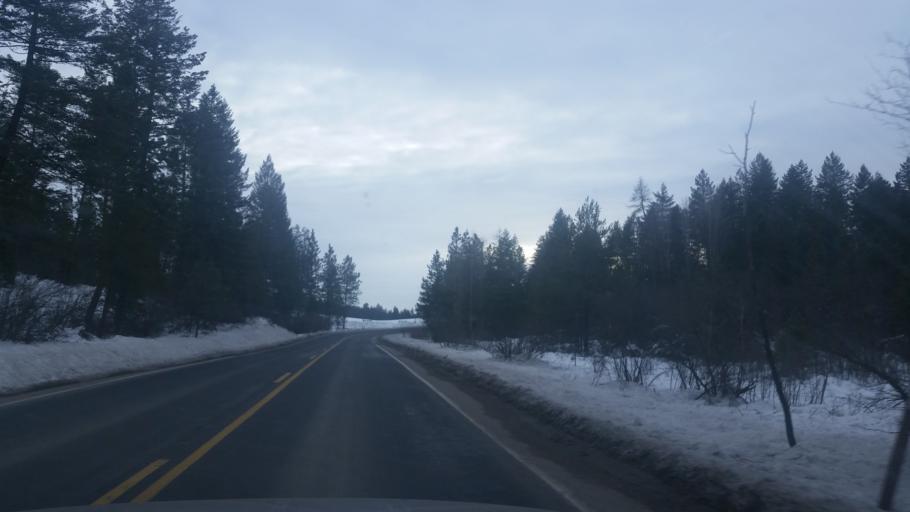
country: US
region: Washington
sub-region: Stevens County
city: Chewelah
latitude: 48.1089
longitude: -117.7557
